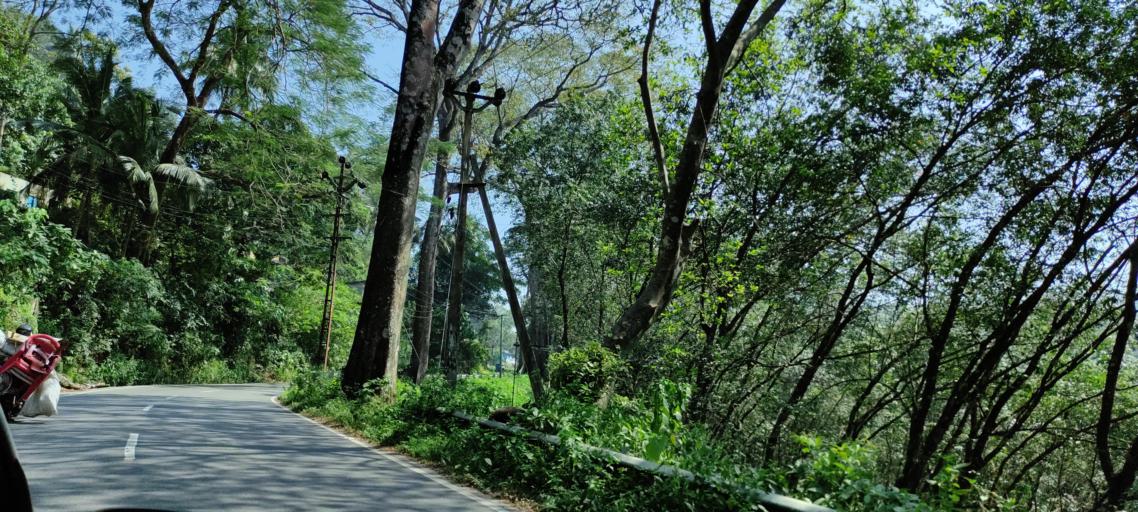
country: IN
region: Kerala
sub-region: Kollam
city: Punalur
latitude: 8.9715
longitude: 77.0669
